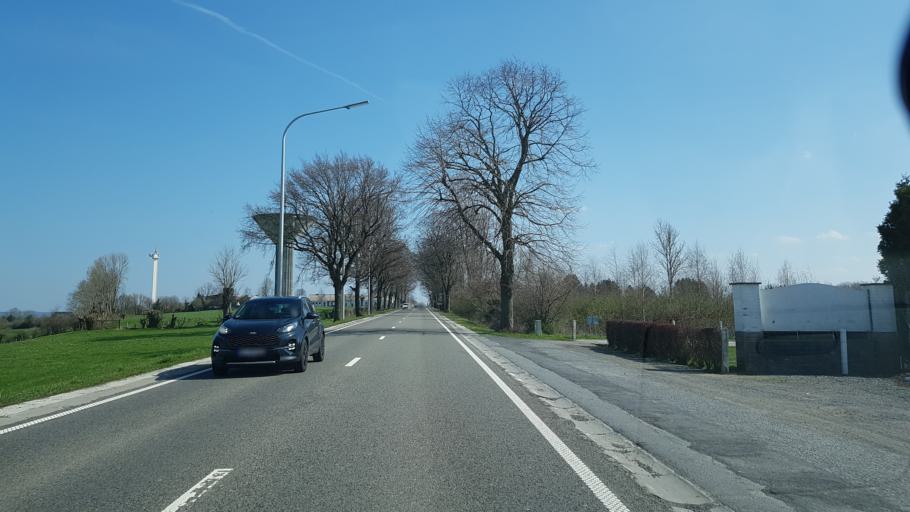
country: BE
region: Wallonia
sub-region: Province de Liege
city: Welkenraedt
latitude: 50.6745
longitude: 5.9152
